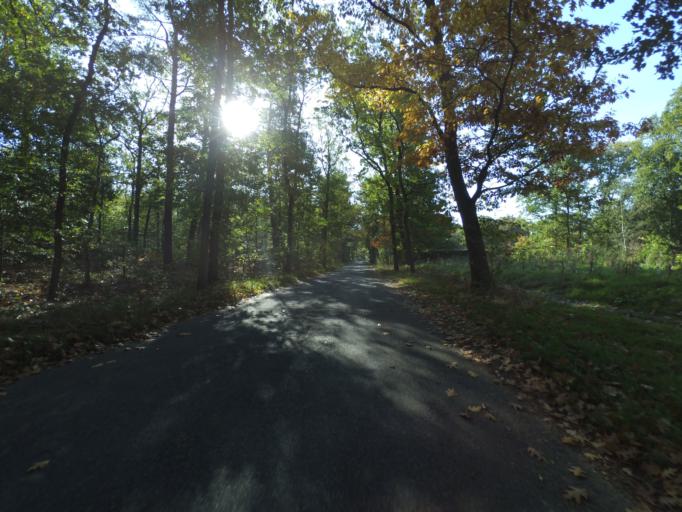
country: NL
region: Utrecht
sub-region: Gemeente Zeist
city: Zeist
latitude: 52.1093
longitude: 5.2281
